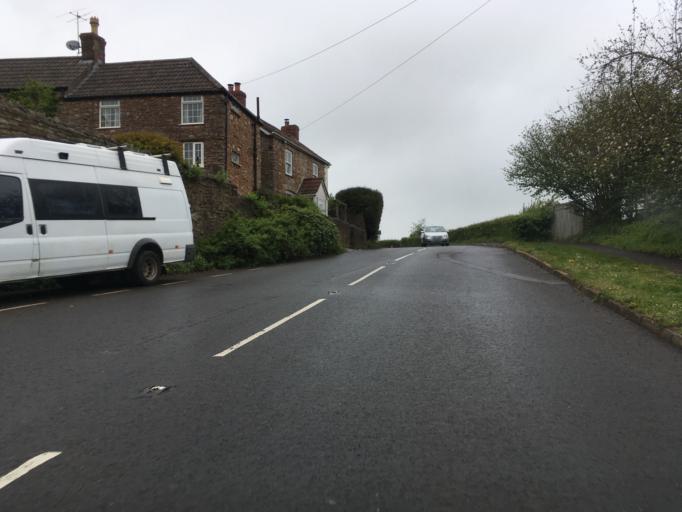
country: GB
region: England
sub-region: North Somerset
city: Blagdon
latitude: 51.3261
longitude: -2.7162
